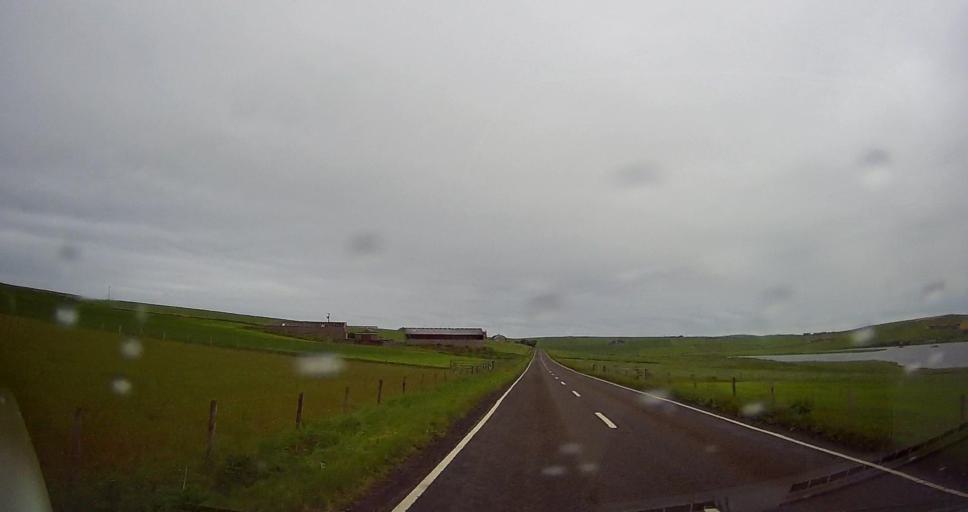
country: GB
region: Scotland
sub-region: Orkney Islands
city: Stromness
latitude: 59.0058
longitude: -3.2901
